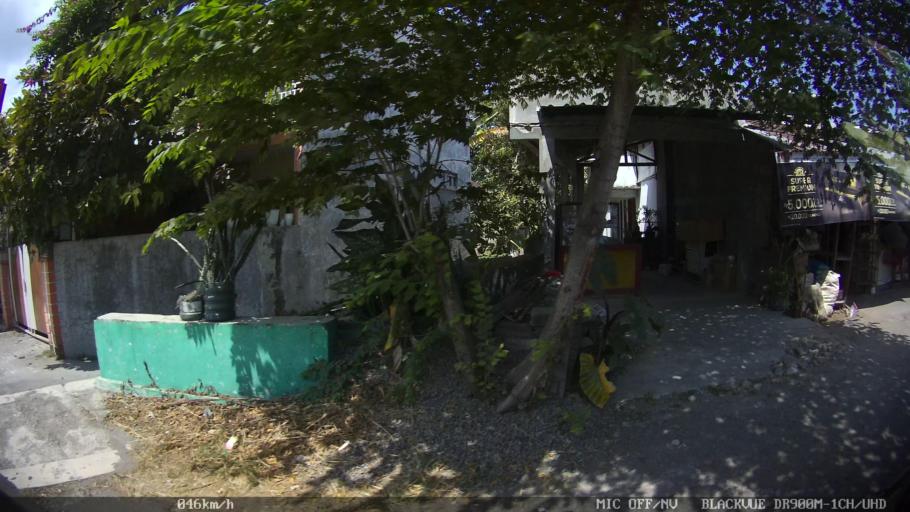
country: ID
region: Daerah Istimewa Yogyakarta
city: Pundong
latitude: -7.9448
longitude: 110.3746
